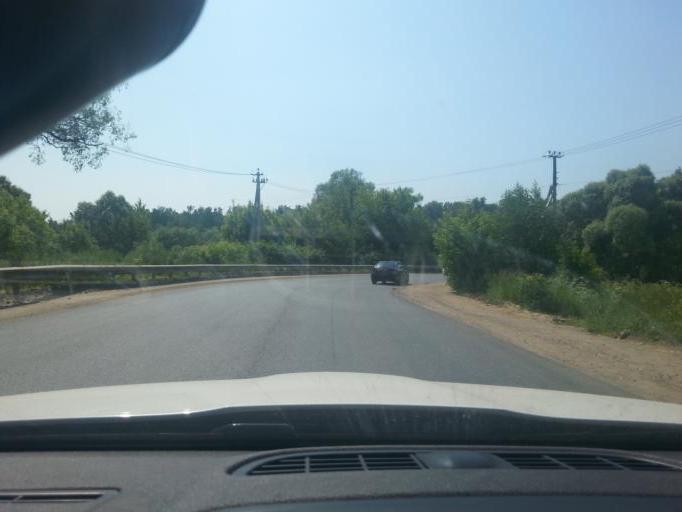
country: RU
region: Moskovskaya
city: Korenevo
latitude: 55.7115
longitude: 37.9723
